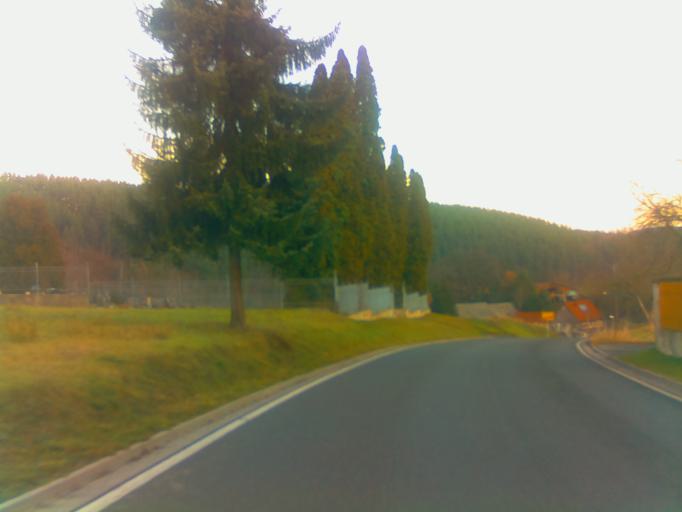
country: DE
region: Thuringia
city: Unterwellenborn
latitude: 50.7024
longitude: 11.4007
